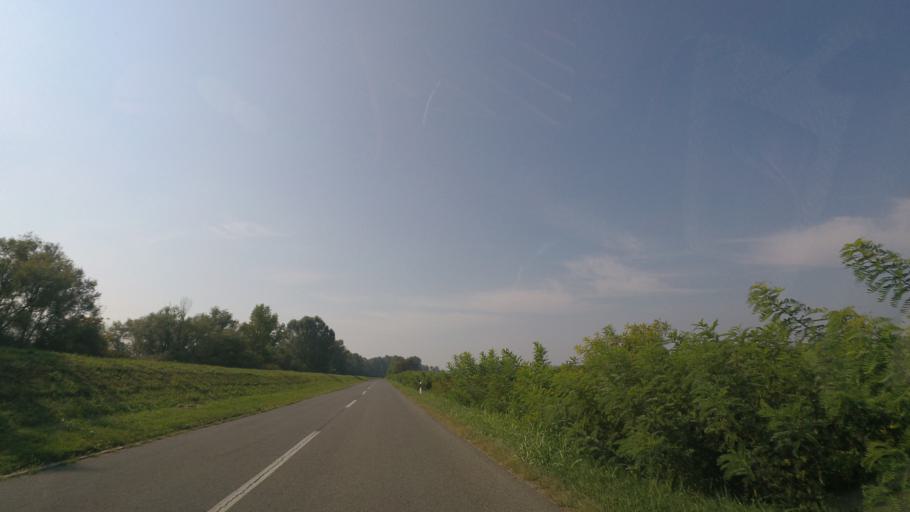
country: BA
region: Republika Srpska
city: Bosanska Dubica
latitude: 45.2241
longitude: 16.8354
